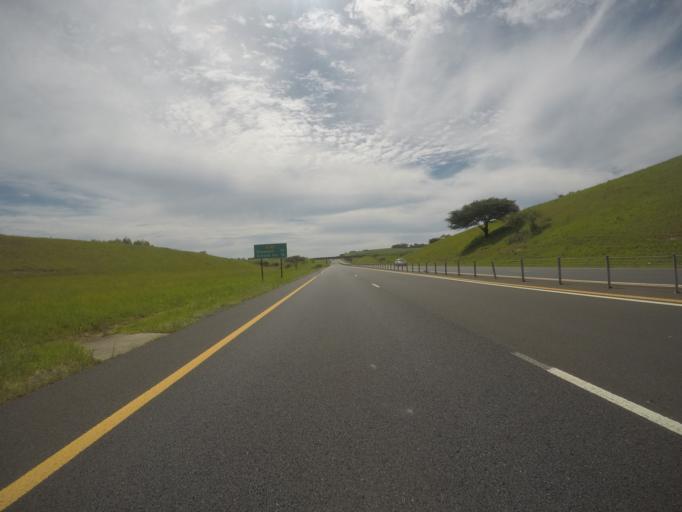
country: ZA
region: KwaZulu-Natal
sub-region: iLembe District Municipality
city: Mandeni
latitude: -29.1795
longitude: 31.4984
